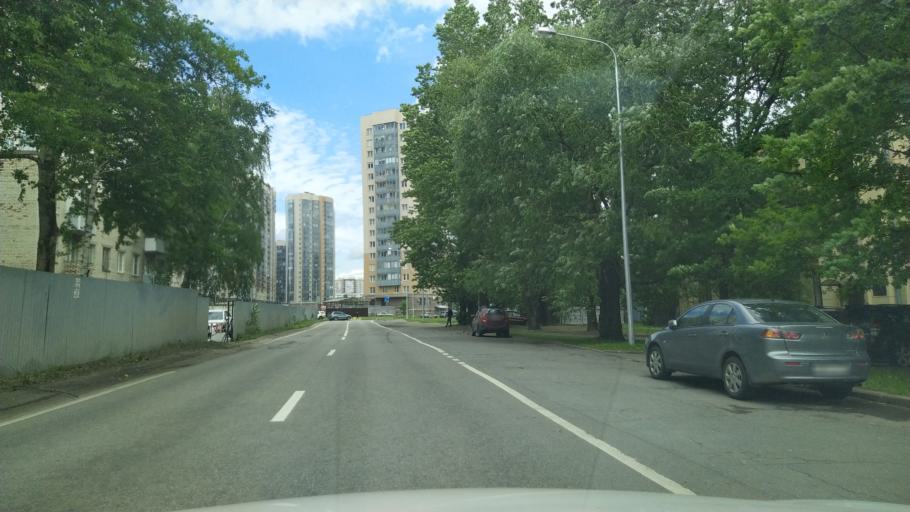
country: RU
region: Leningrad
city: Akademicheskoe
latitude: 60.0093
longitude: 30.3864
